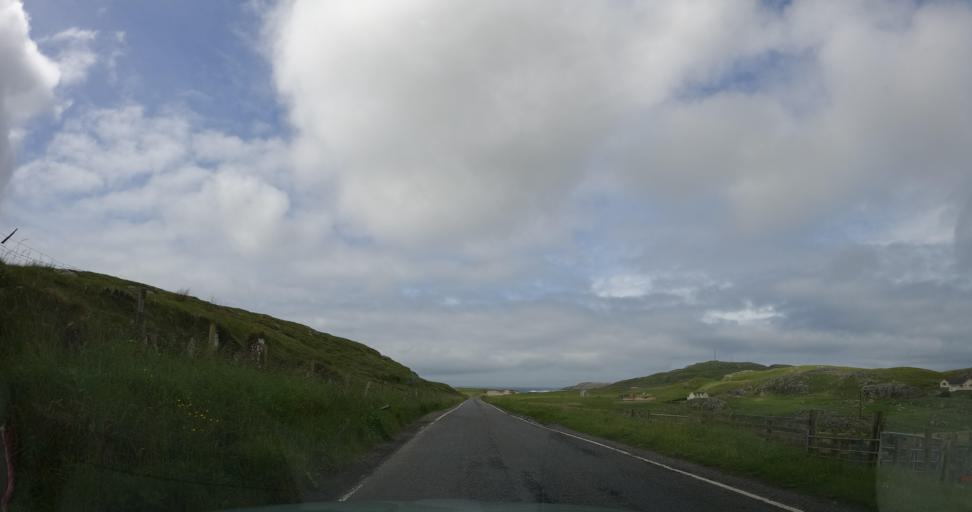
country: GB
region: Scotland
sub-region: Eilean Siar
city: Barra
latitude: 57.0027
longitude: -7.4917
